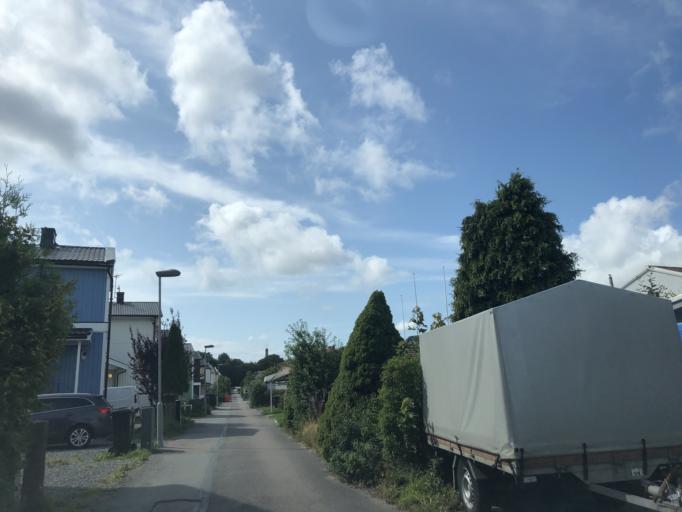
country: SE
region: Vaestra Goetaland
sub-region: Goteborg
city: Majorna
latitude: 57.7060
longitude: 11.8981
